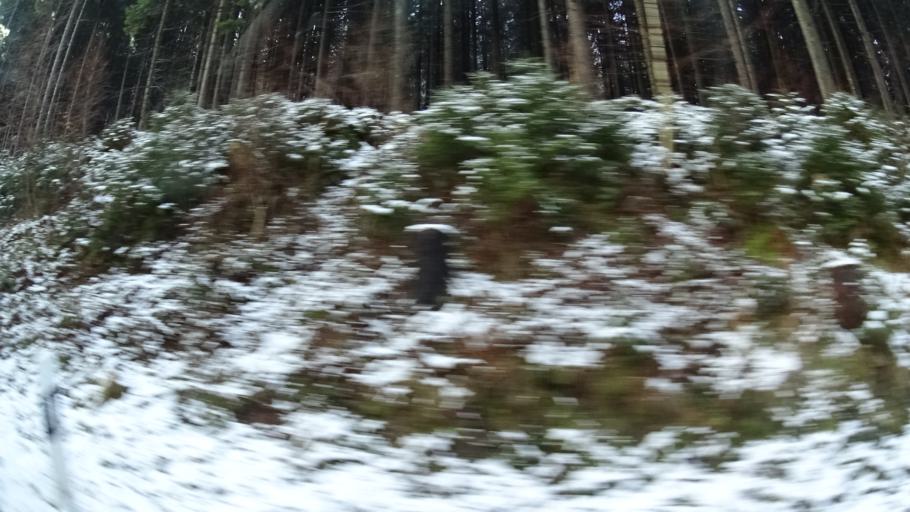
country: DE
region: Thuringia
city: Frankenhain
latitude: 50.7621
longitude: 10.7700
